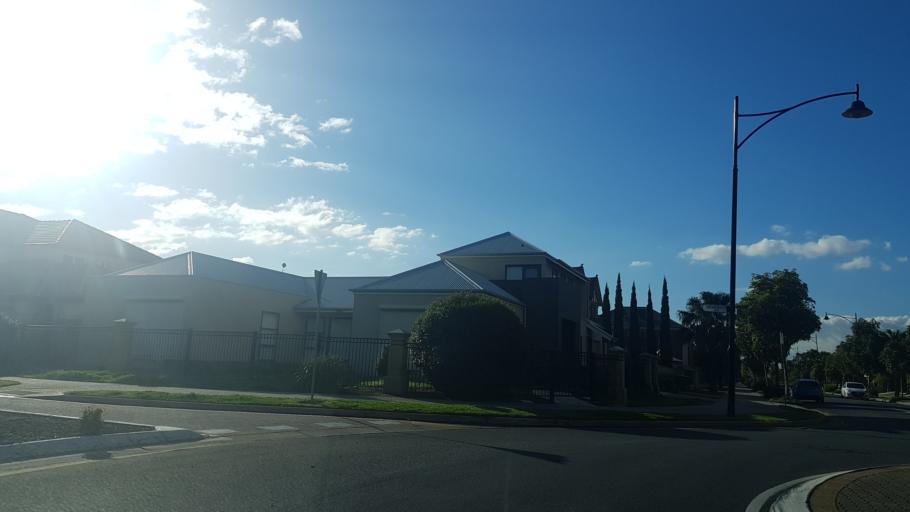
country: AU
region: South Australia
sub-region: Salisbury
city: Ingle Farm
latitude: -34.8165
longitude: 138.6077
